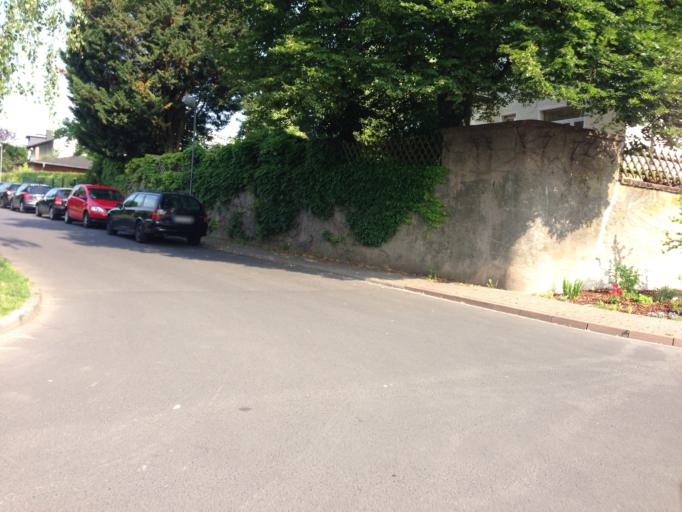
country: DE
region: Hesse
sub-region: Regierungsbezirk Darmstadt
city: Muehlheim am Main
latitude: 50.1310
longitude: 8.8369
